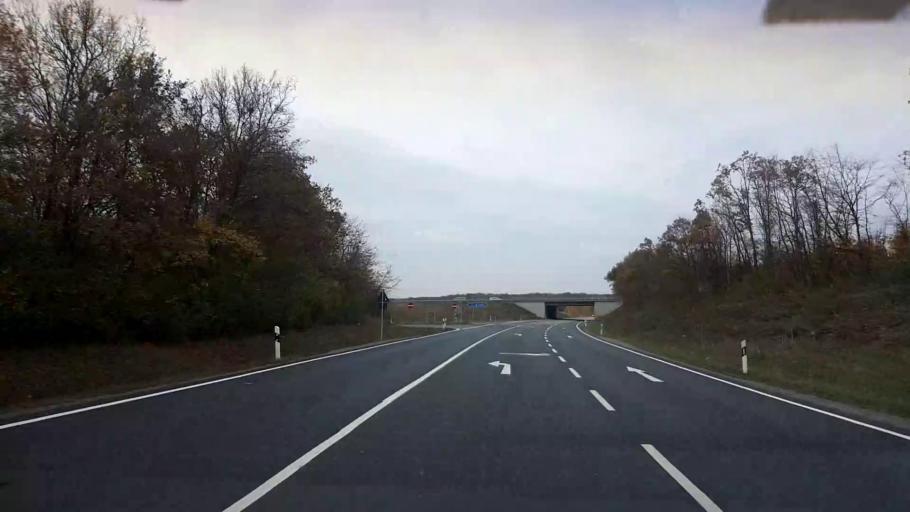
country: DE
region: Bavaria
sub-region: Regierungsbezirk Unterfranken
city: Wiesentheid
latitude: 49.7728
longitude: 10.3458
